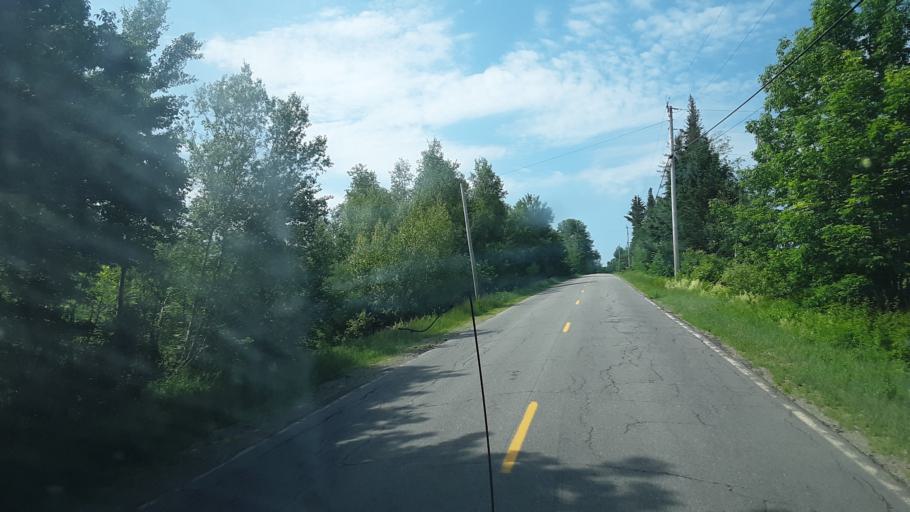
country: US
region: Maine
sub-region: Waldo County
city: Frankfort
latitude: 44.5821
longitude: -68.9470
